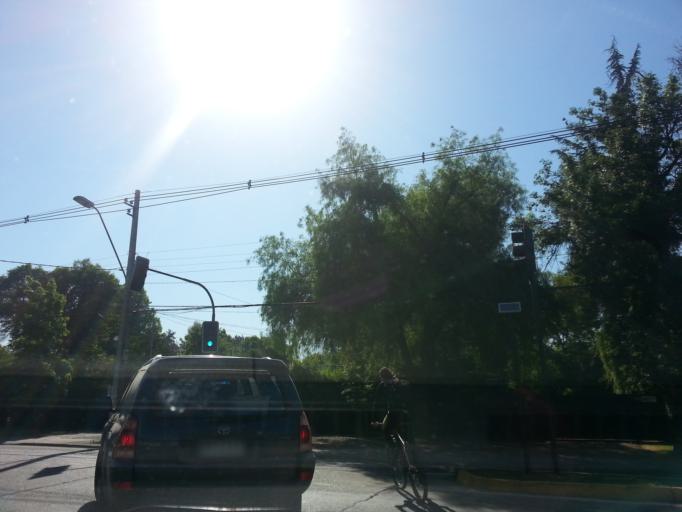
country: CL
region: Santiago Metropolitan
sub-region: Provincia de Santiago
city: Villa Presidente Frei, Nunoa, Santiago, Chile
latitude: -33.3894
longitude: -70.5956
